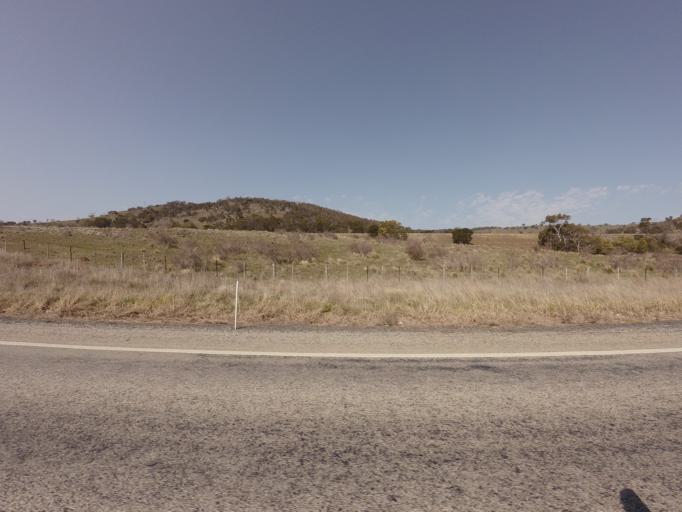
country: AU
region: Tasmania
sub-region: Northern Midlands
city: Evandale
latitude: -41.8174
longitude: 147.5493
